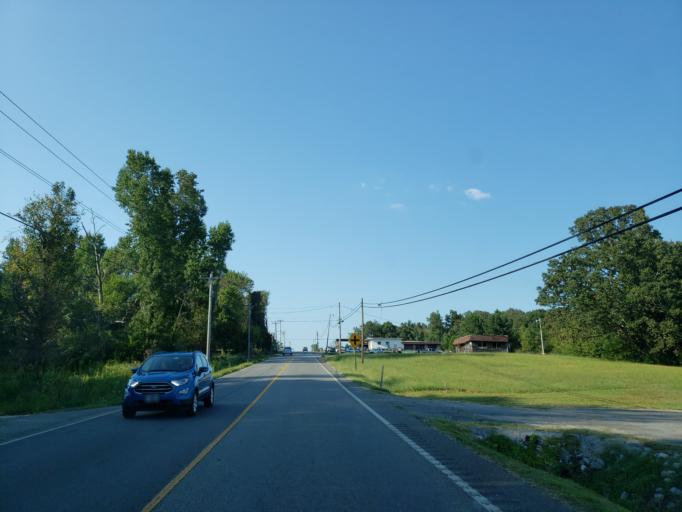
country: US
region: Tennessee
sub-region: Bradley County
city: Wildwood Lake
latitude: 35.0301
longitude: -84.7325
